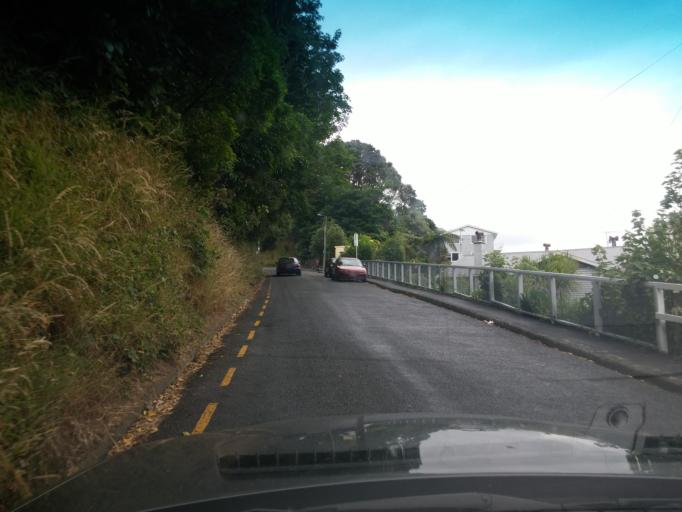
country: NZ
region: Wellington
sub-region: Wellington City
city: Kelburn
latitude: -41.2820
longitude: 174.7635
